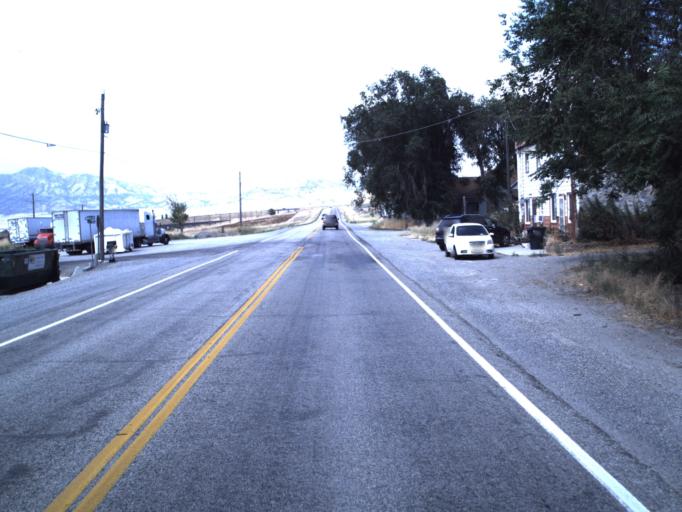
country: US
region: Utah
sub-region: Box Elder County
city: Garland
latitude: 41.7745
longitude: -112.0954
